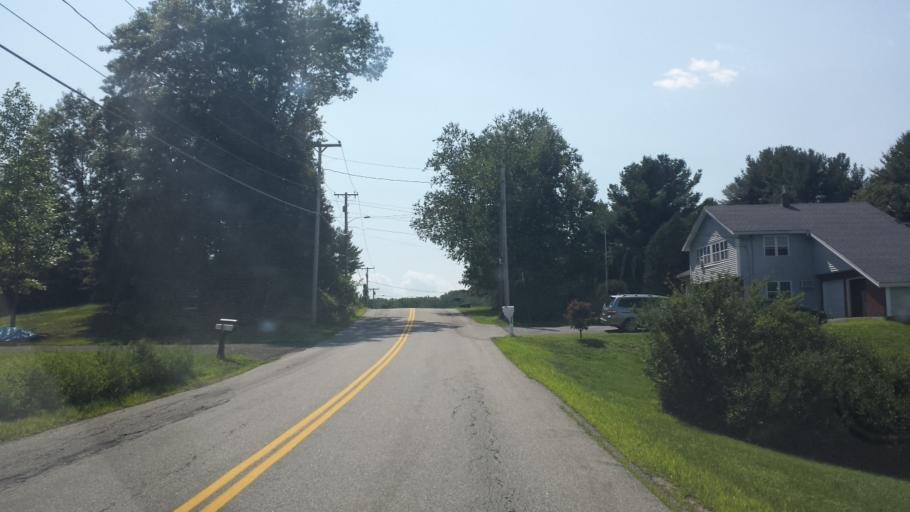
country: US
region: Maine
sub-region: York County
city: Biddeford
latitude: 43.4688
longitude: -70.5032
